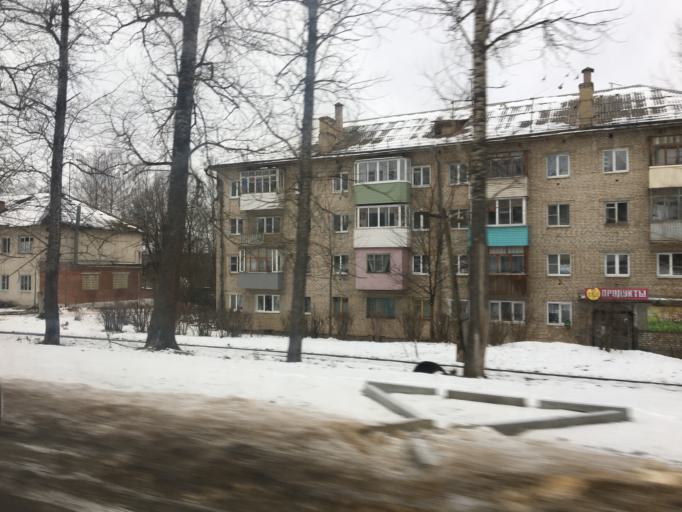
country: RU
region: Tula
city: Kosaya Gora
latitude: 54.0785
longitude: 37.5425
